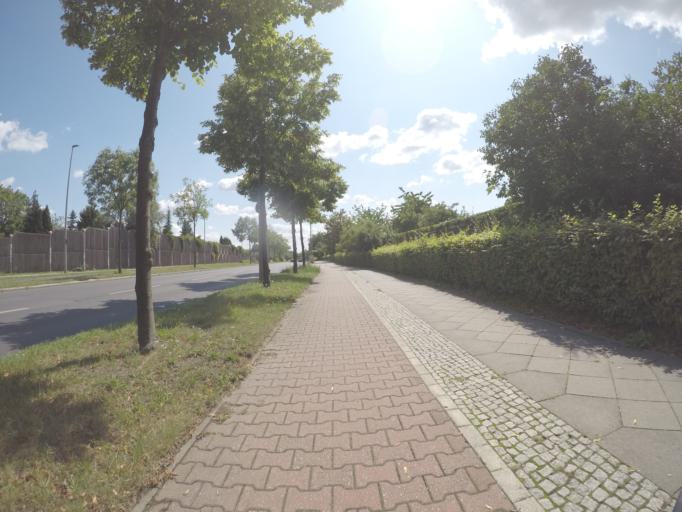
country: DE
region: Berlin
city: Marzahn
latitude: 52.5309
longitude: 13.5653
